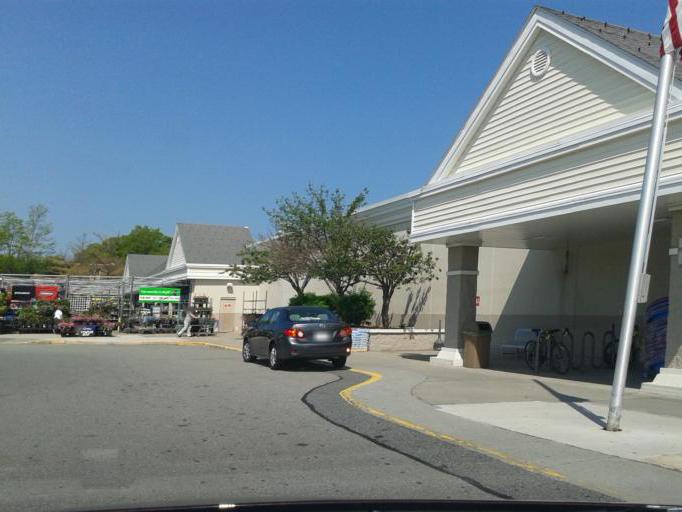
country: US
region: Massachusetts
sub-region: Middlesex County
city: Framingham
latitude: 42.3004
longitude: -71.3994
